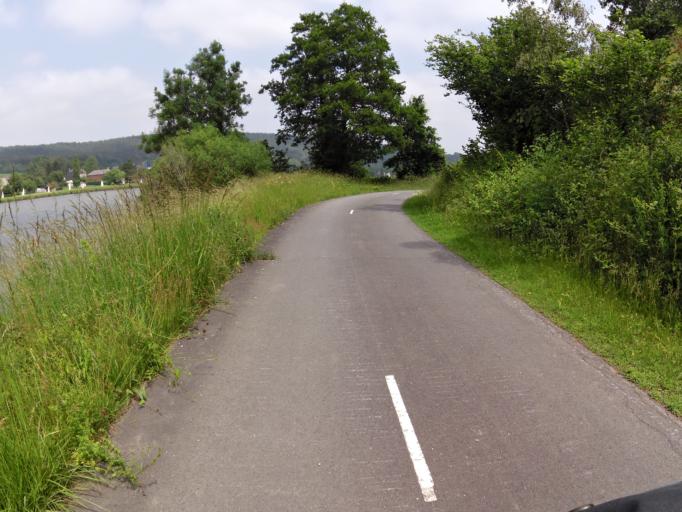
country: BE
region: Wallonia
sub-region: Province de Namur
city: Doische
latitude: 50.1054
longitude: 4.7672
